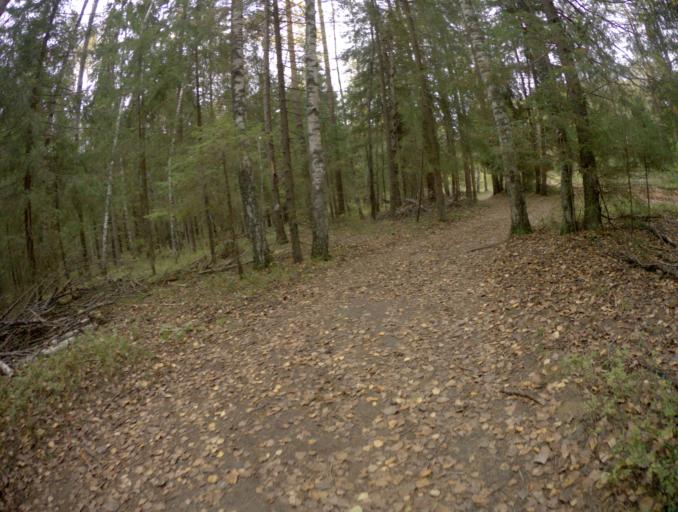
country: RU
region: Vladimir
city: Stepantsevo
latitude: 56.3057
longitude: 41.7185
